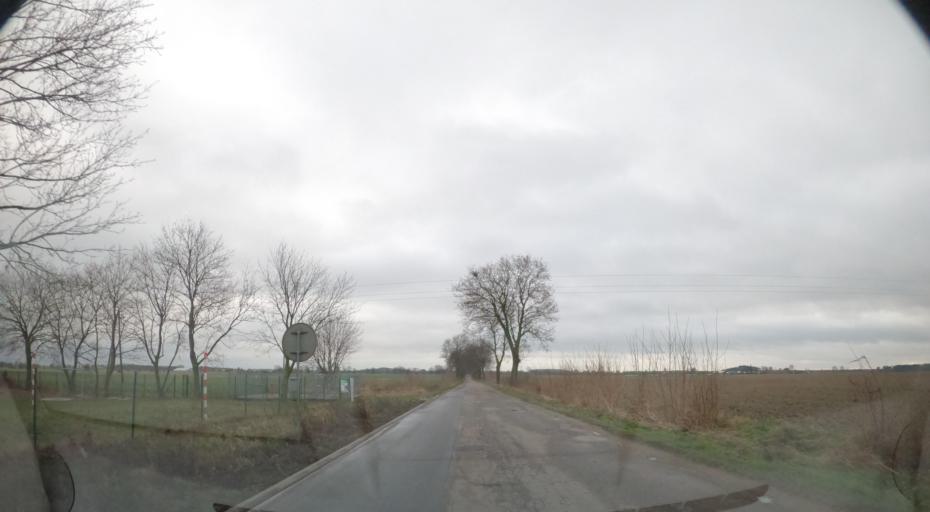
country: PL
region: Greater Poland Voivodeship
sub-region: Powiat pilski
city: Wysoka
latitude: 53.2693
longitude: 17.1063
